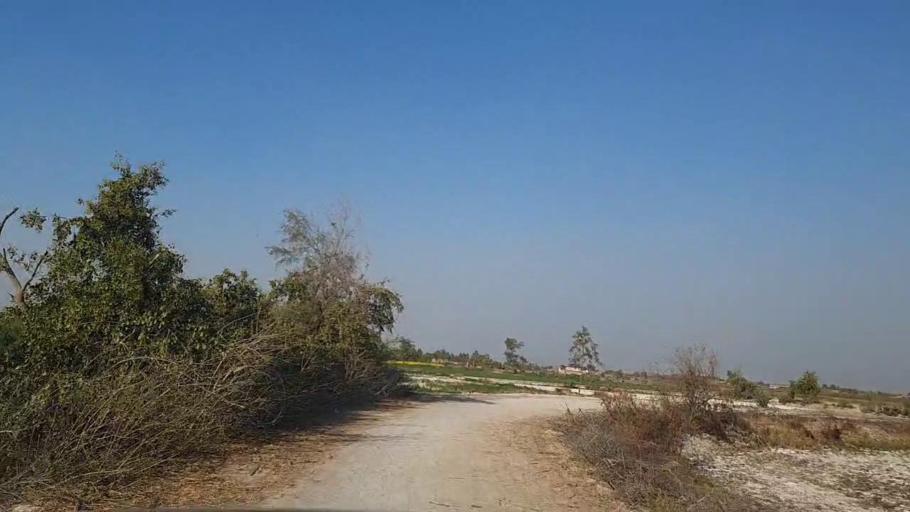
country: PK
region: Sindh
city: Daur
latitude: 26.3204
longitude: 68.1782
